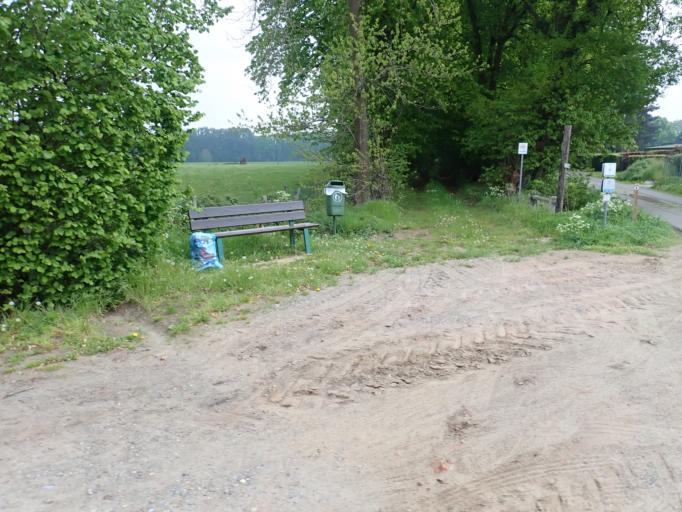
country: BE
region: Flanders
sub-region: Provincie Antwerpen
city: Grobbendonk
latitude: 51.2096
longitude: 4.7168
